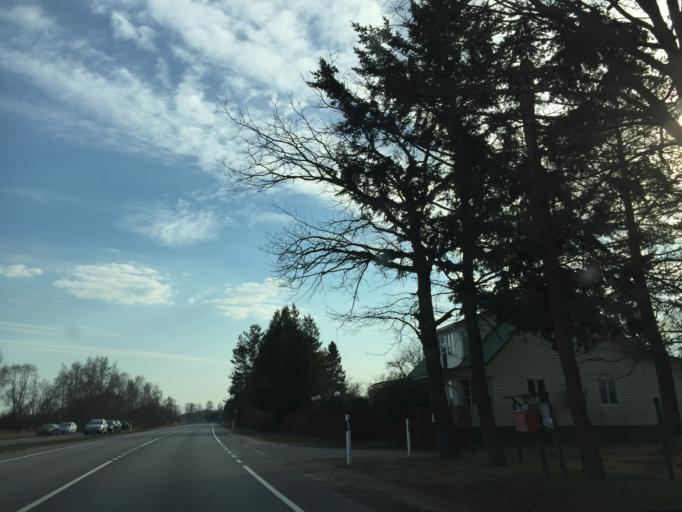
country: EE
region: Jogevamaa
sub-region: Mustvee linn
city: Mustvee
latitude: 58.9192
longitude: 27.0090
